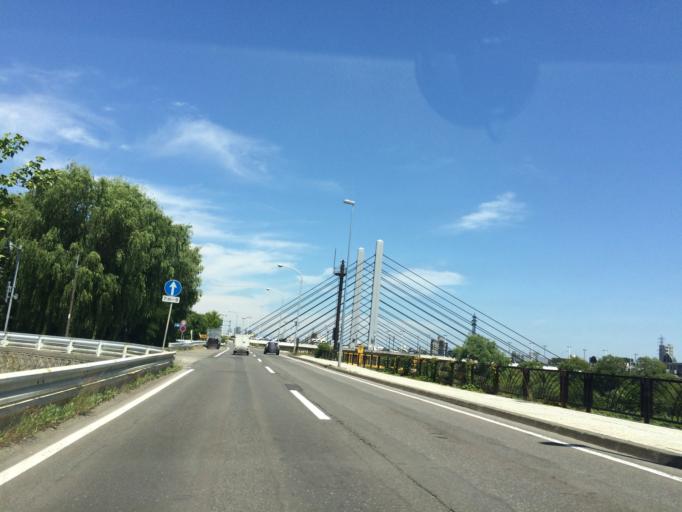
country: JP
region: Hokkaido
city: Sapporo
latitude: 43.0146
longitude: 141.3519
